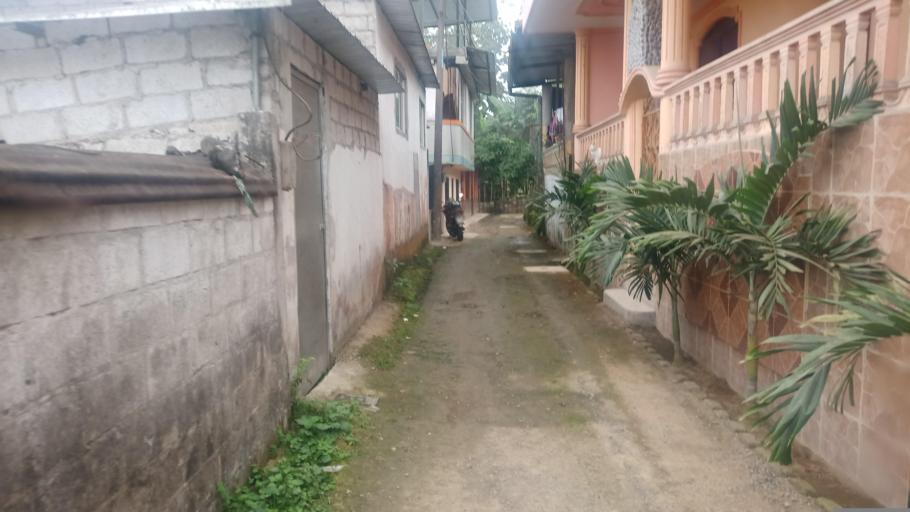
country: EC
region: Santo Domingo de los Tsachilas
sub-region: Canton Santo Domingo de los Colorados
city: Santo Domingo de los Colorados
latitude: -0.2588
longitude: -79.1197
